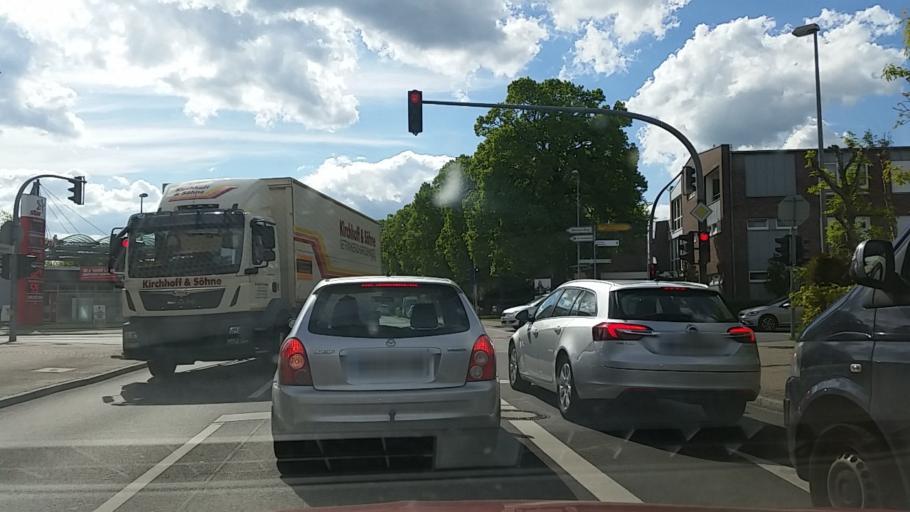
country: DE
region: Schleswig-Holstein
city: Ahrensburg
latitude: 53.6757
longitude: 10.2374
